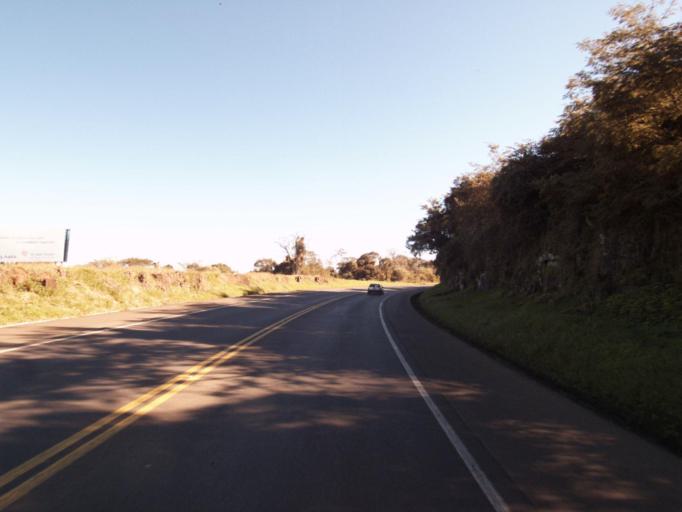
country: BR
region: Santa Catarina
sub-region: Chapeco
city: Chapeco
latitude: -26.9659
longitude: -52.5670
